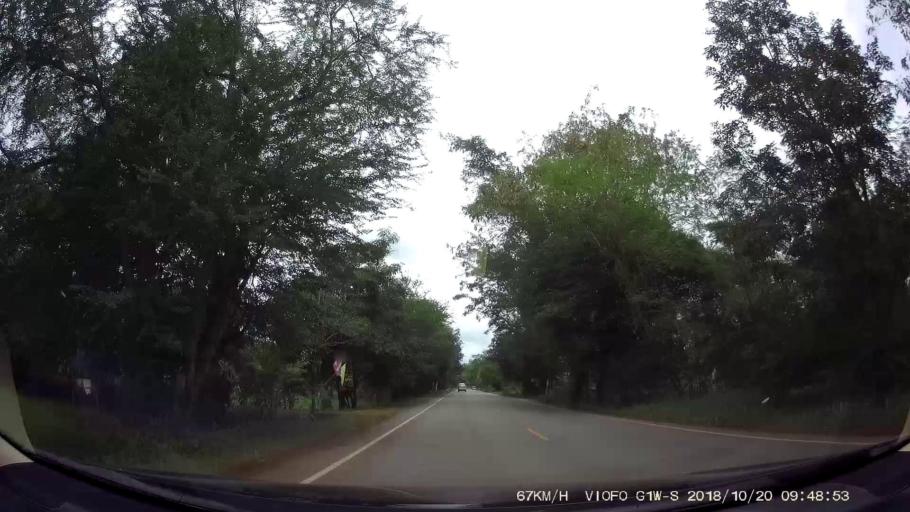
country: TH
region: Chaiyaphum
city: Khon San
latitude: 16.5147
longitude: 101.9087
